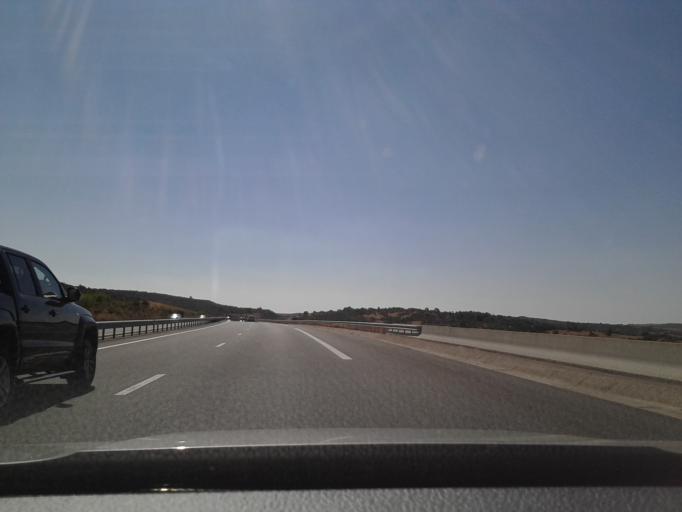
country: FR
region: Midi-Pyrenees
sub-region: Departement de l'Aveyron
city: Creissels
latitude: 44.0581
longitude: 3.0331
